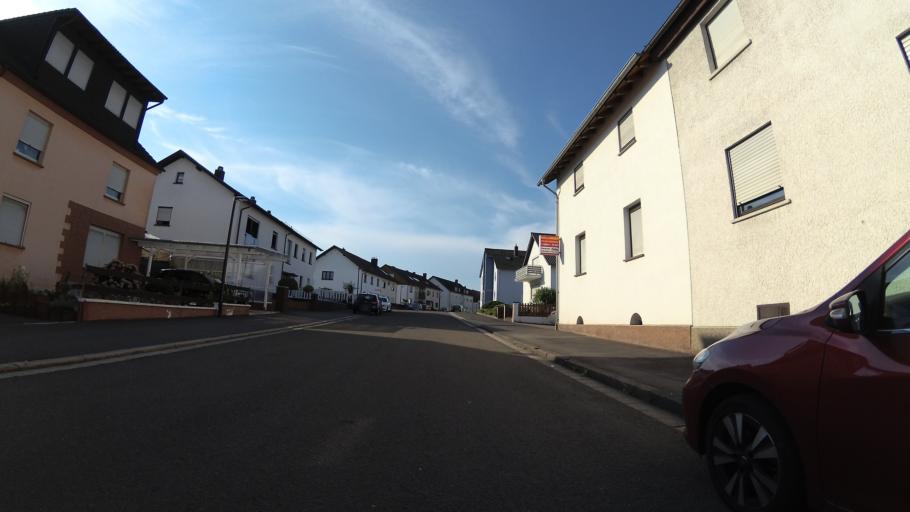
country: DE
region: Saarland
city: Homburg
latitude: 49.3357
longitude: 7.3303
